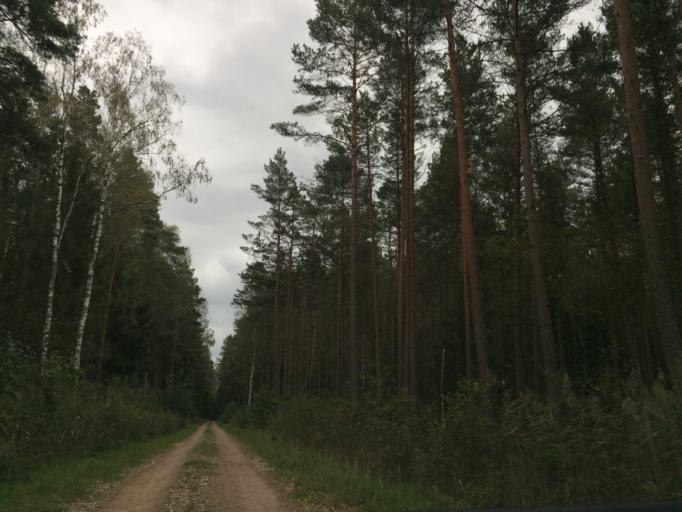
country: LV
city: Tireli
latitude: 56.8905
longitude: 23.5430
